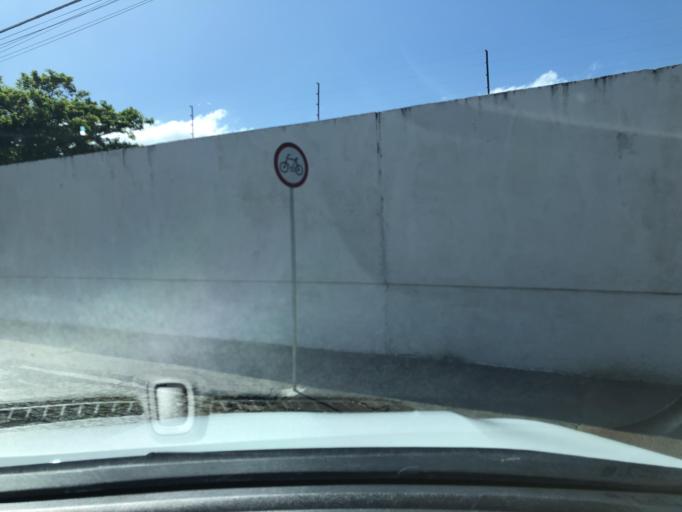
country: BR
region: Santa Catarina
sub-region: Joinville
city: Joinville
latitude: -26.2688
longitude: -48.8492
